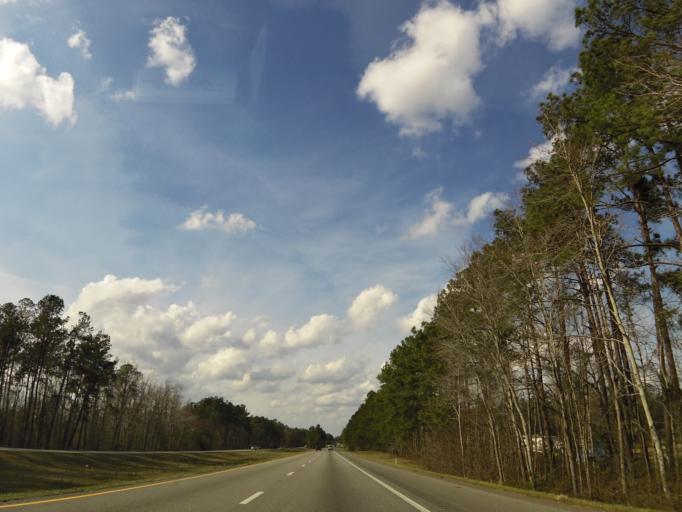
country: US
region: South Carolina
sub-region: Dorchester County
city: Ridgeville
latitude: 33.1816
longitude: -80.3786
